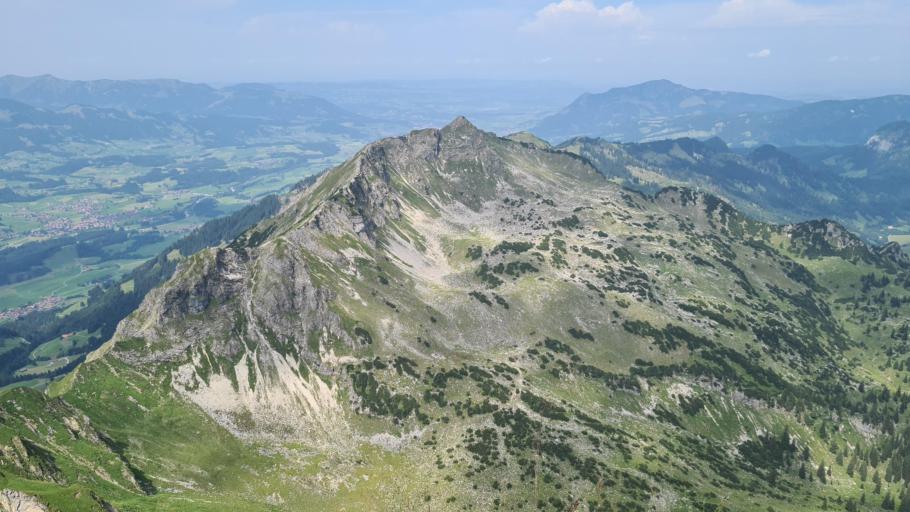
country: DE
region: Bavaria
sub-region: Swabia
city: Oberstdorf
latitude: 47.4221
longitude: 10.3398
